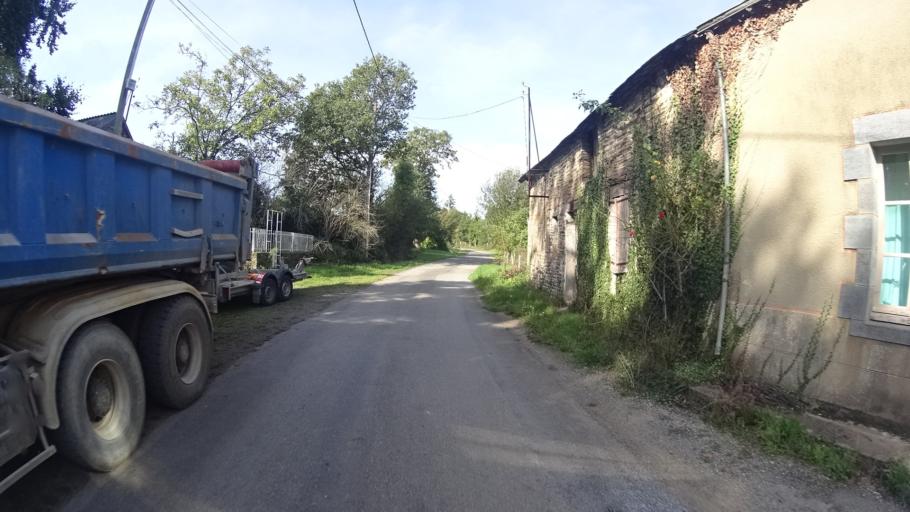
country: FR
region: Brittany
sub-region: Departement du Morbihan
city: Saint-Martin-sur-Oust
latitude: 47.7559
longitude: -2.2134
